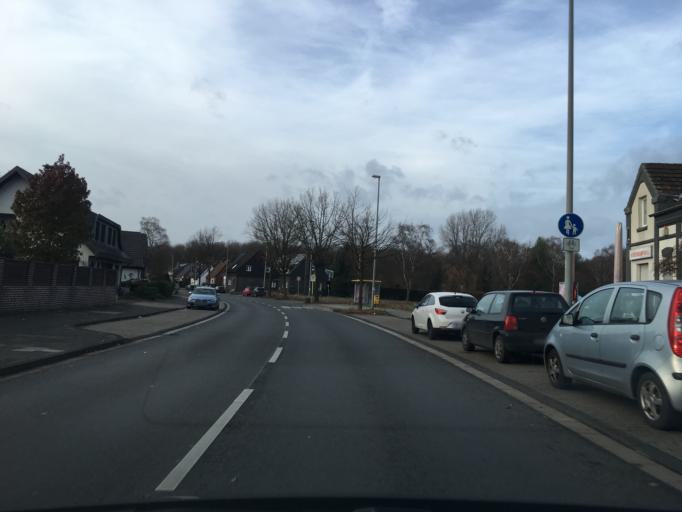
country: DE
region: North Rhine-Westphalia
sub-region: Regierungsbezirk Dusseldorf
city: Oberhausen
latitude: 51.5559
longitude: 6.8412
